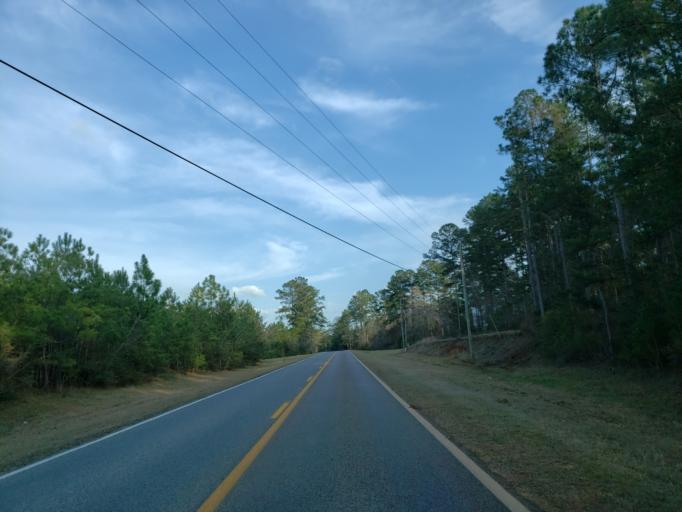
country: US
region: Mississippi
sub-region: Clarke County
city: Stonewall
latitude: 32.1751
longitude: -88.7904
